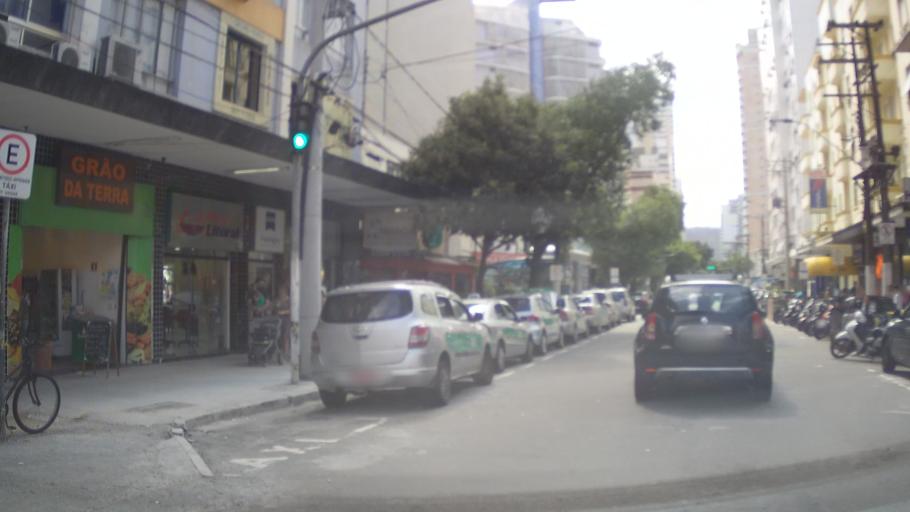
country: BR
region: Sao Paulo
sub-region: Santos
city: Santos
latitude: -23.9670
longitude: -46.3332
